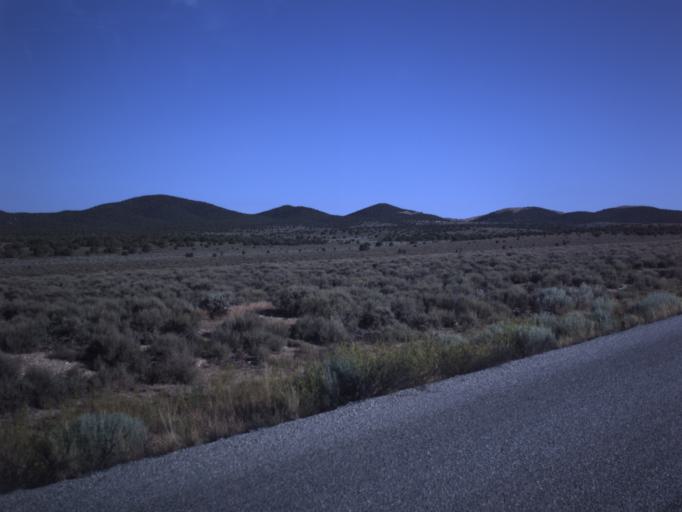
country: US
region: Utah
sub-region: Iron County
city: Enoch
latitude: 38.0121
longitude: -112.9979
